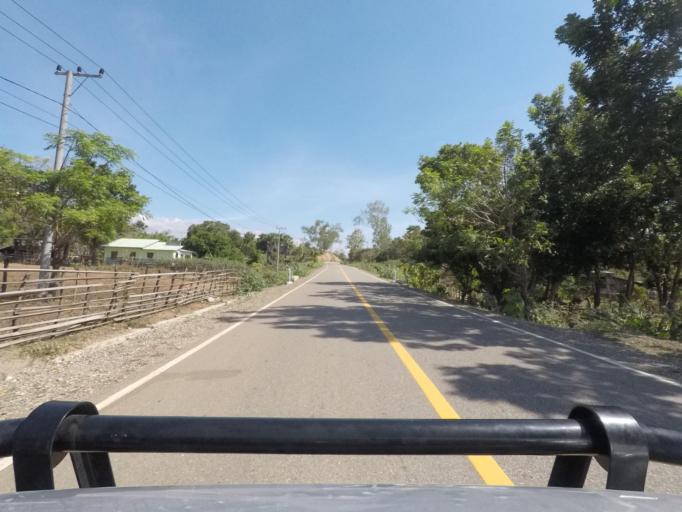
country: TL
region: Bobonaro
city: Maliana
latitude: -8.8876
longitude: 125.0241
